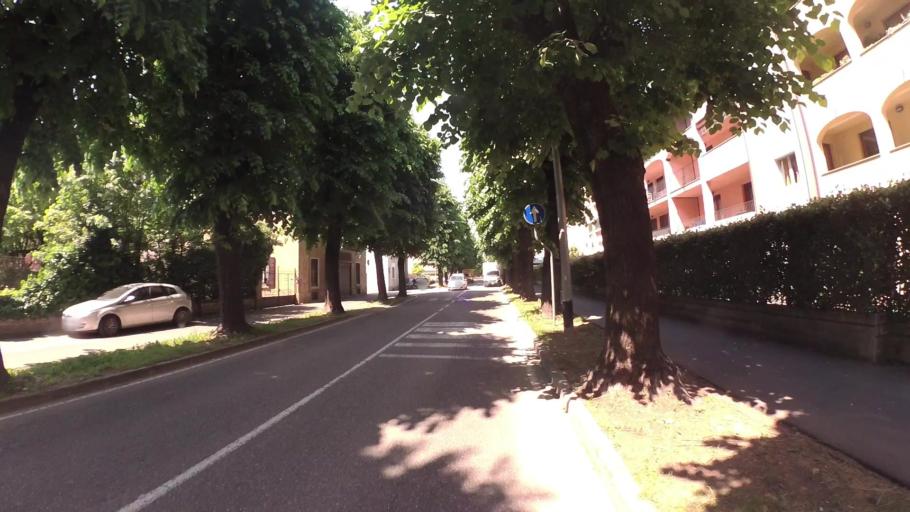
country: IT
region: Lombardy
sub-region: Provincia di Varese
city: Tradate
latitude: 45.7063
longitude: 8.9133
